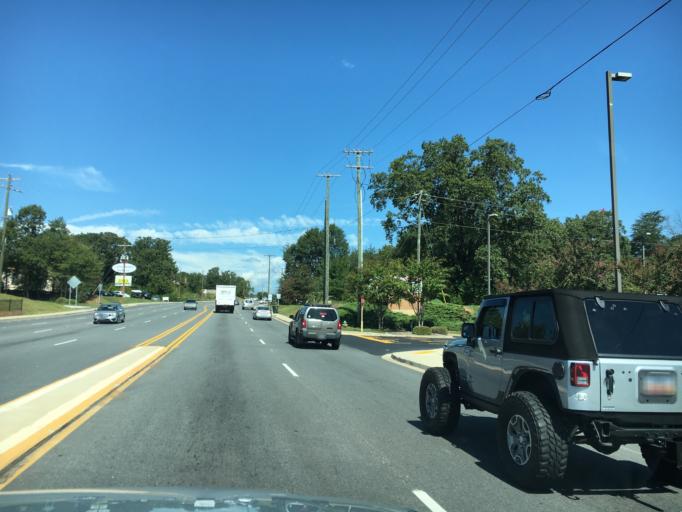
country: US
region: South Carolina
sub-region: Greenville County
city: Greer
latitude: 34.9428
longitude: -82.2592
